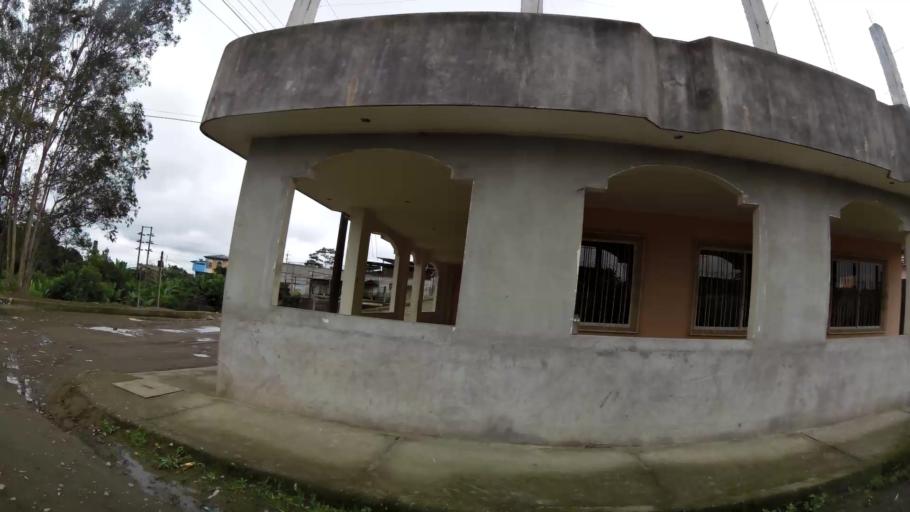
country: EC
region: Santo Domingo de los Tsachilas
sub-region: Canton Santo Domingo de los Colorados
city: Santo Domingo de los Colorados
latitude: -0.2489
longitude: -79.1993
